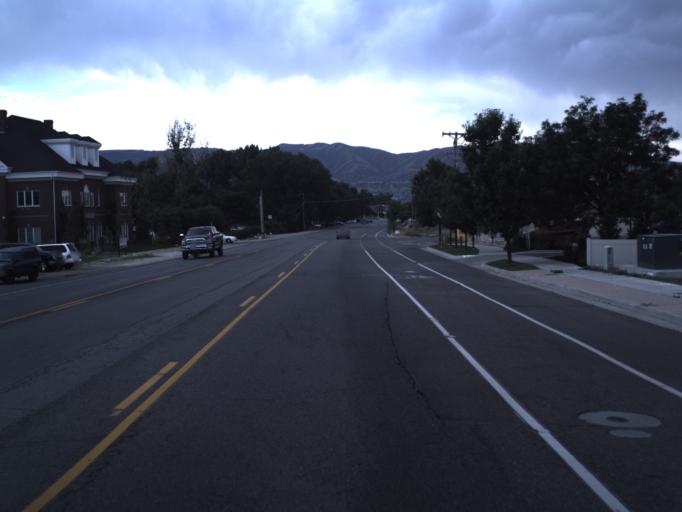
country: US
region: Utah
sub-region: Salt Lake County
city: Draper
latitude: 40.5399
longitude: -111.8714
